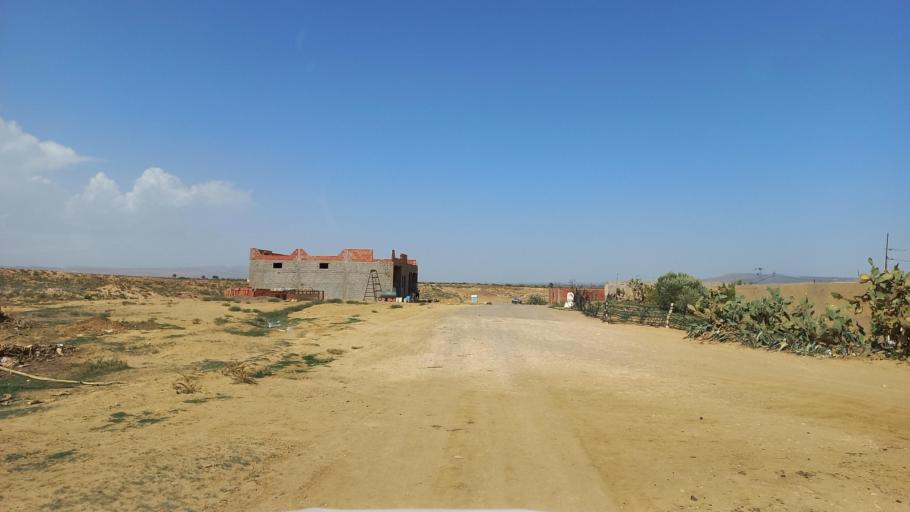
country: TN
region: Al Qasrayn
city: Kasserine
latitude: 35.2015
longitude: 9.0366
